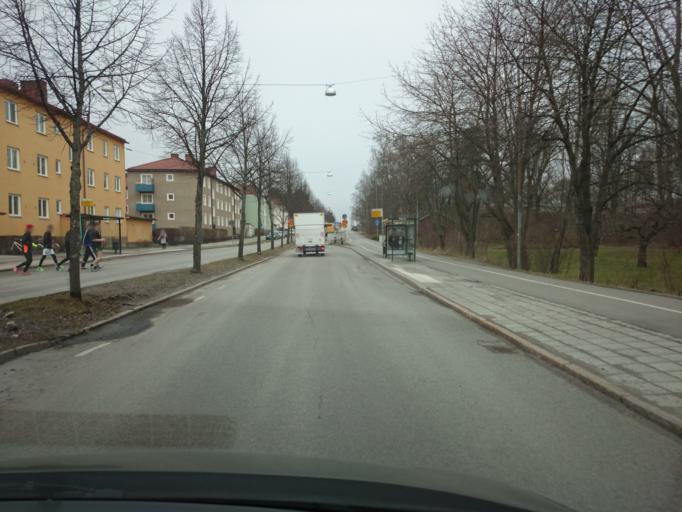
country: SE
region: Uppsala
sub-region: Uppsala Kommun
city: Uppsala
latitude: 59.8752
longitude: 17.6248
